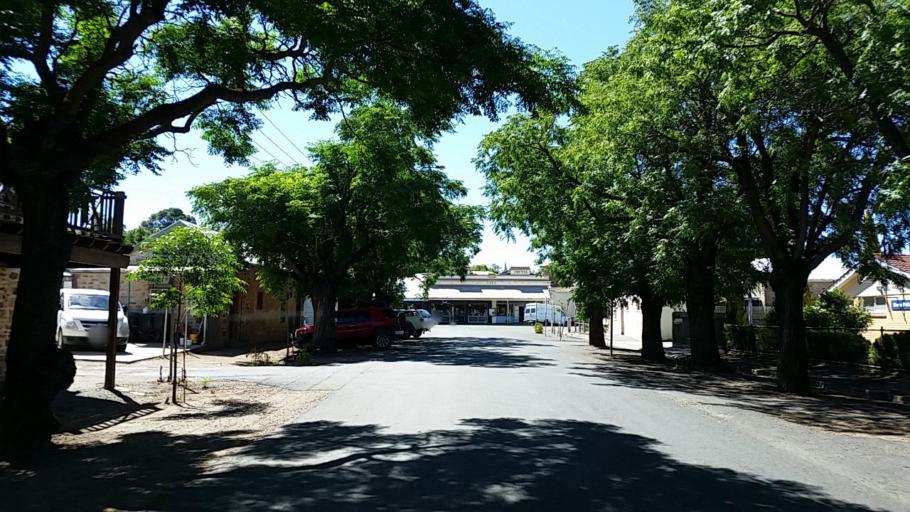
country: AU
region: South Australia
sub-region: Clare and Gilbert Valleys
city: Clare
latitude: -33.6831
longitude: 138.9389
